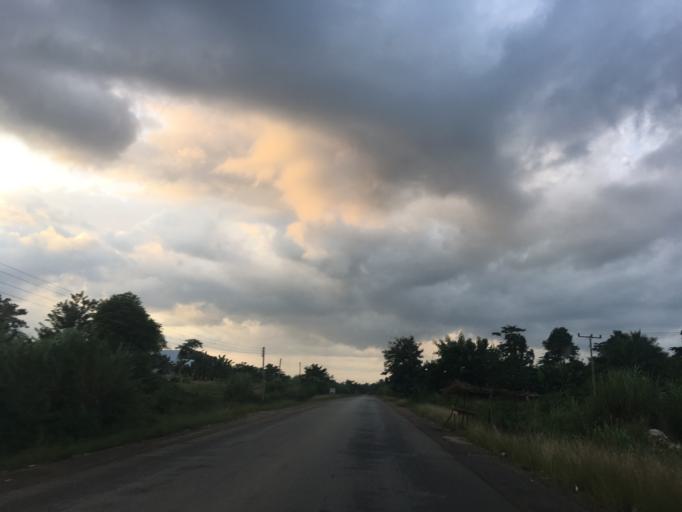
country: GH
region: Western
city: Bibiani
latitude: 6.7542
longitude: -2.5044
